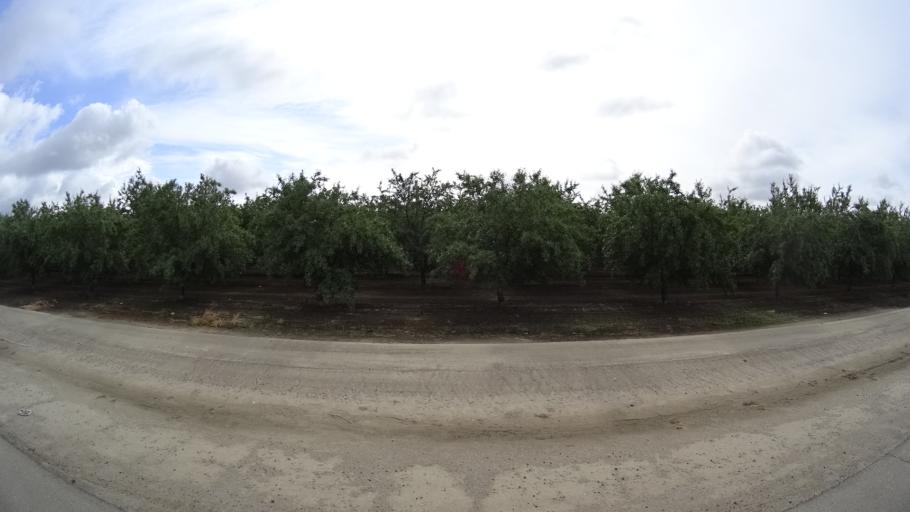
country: US
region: California
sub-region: Kings County
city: Armona
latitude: 36.3406
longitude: -119.6819
